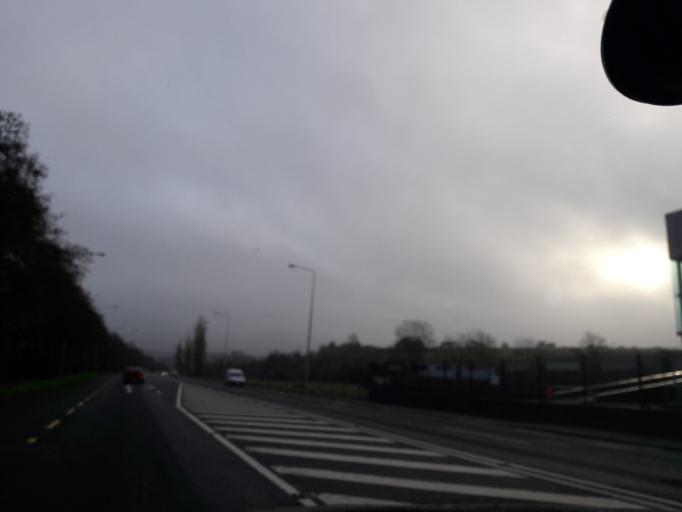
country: IE
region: Ulster
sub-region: County Donegal
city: Letterkenny
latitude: 54.9468
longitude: -7.7089
